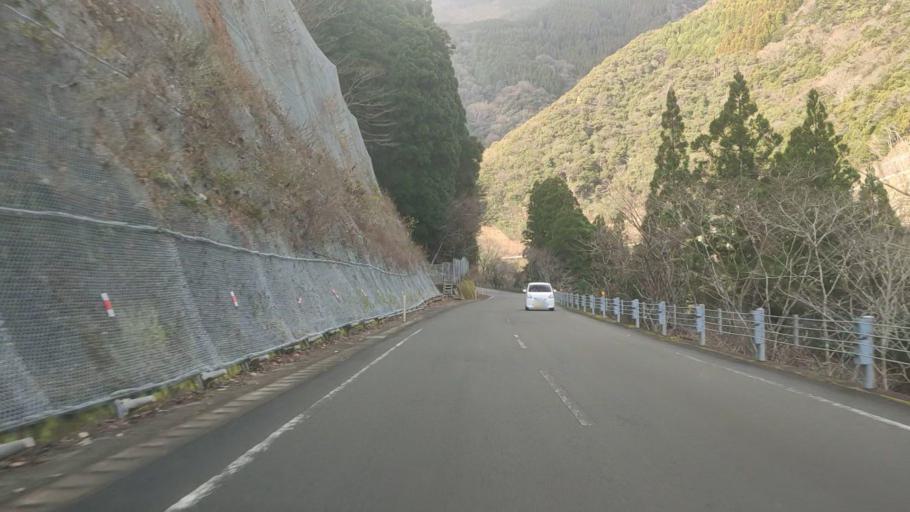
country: JP
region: Kumamoto
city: Hitoyoshi
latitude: 32.4107
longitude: 130.8345
